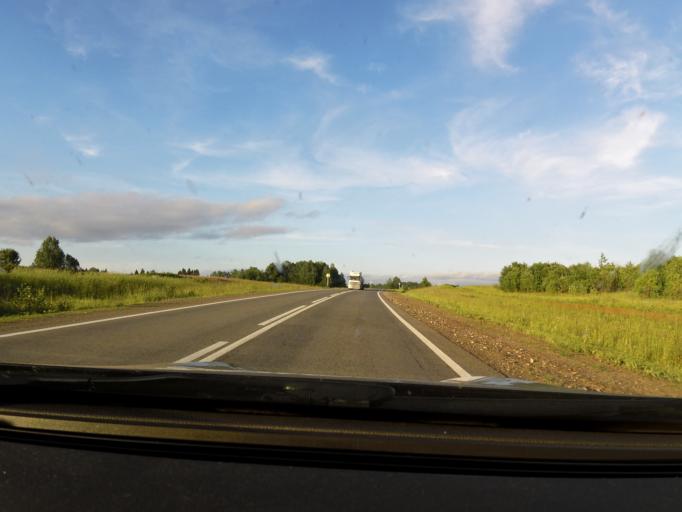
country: RU
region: Perm
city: Siva
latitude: 58.4893
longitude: 54.1095
